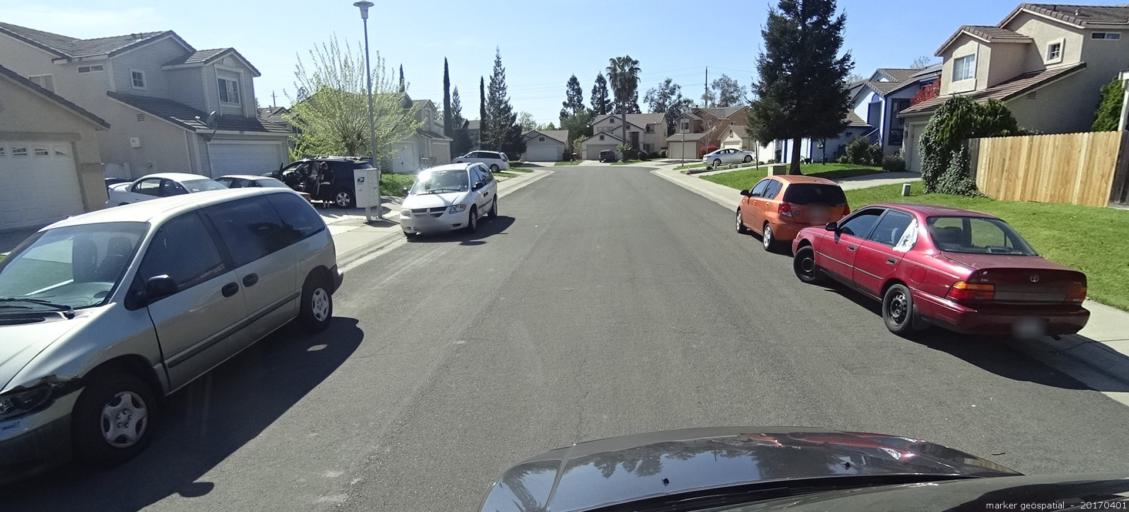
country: US
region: California
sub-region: Sacramento County
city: Laguna
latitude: 38.4483
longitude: -121.4430
